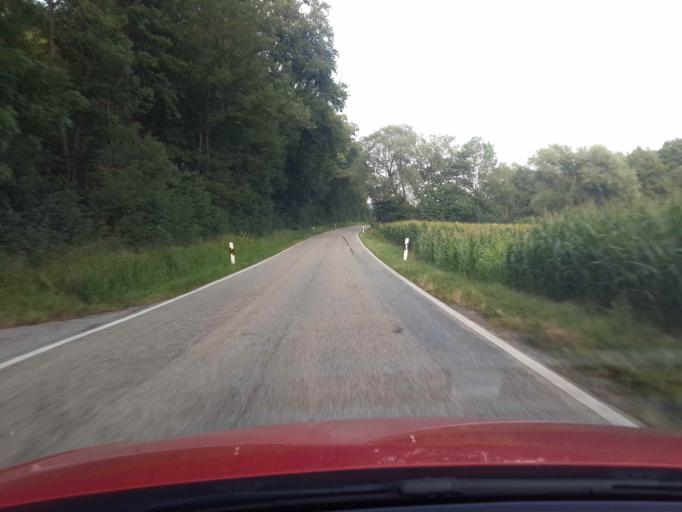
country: DE
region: Baden-Wuerttemberg
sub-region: Regierungsbezirk Stuttgart
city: Zaberfeld
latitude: 49.0186
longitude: 8.9426
